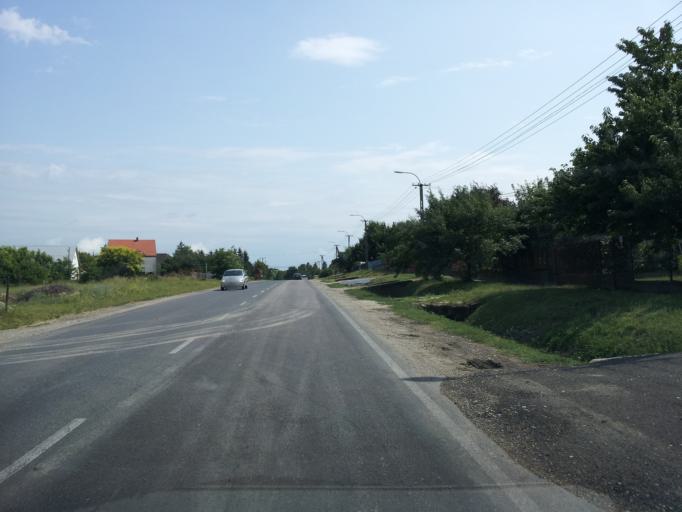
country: HU
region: Fejer
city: Enying
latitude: 46.9431
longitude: 18.2311
